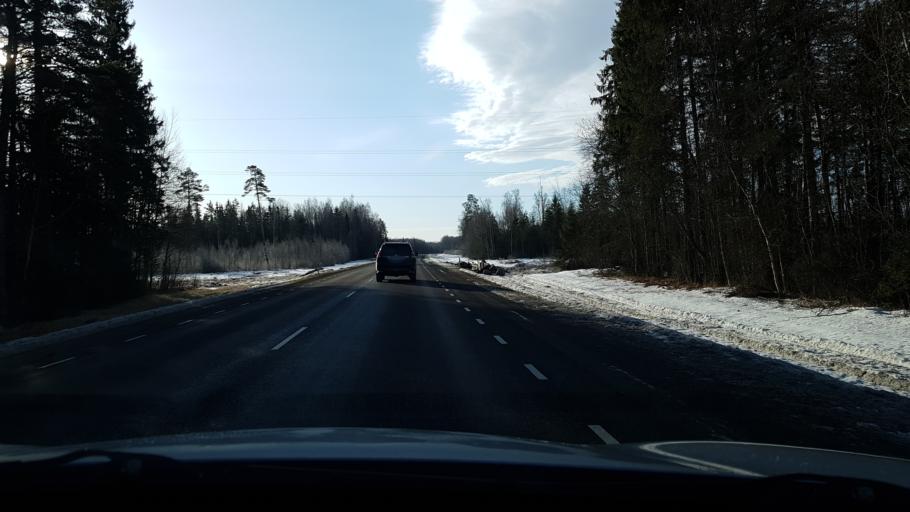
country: EE
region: Viljandimaa
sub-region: Vohma linn
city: Vohma
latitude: 58.6114
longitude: 25.5716
